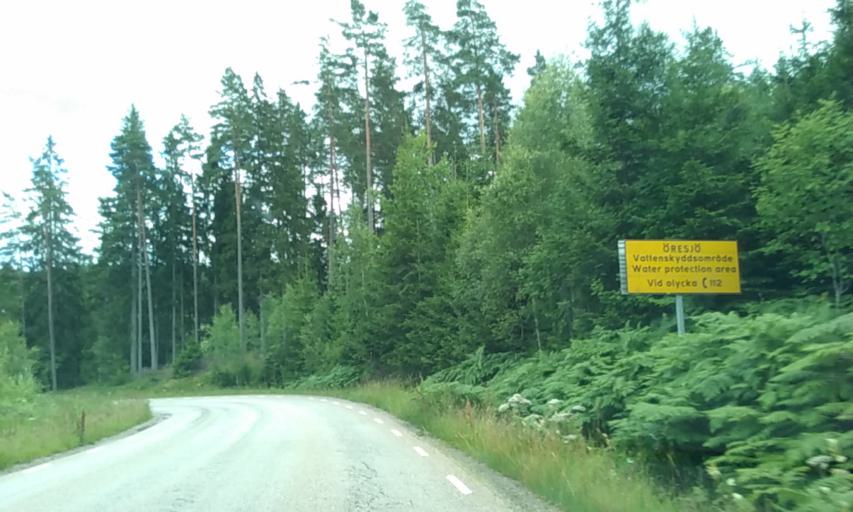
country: SE
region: Vaestra Goetaland
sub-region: Boras Kommun
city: Boras
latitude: 57.8144
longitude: 12.9338
